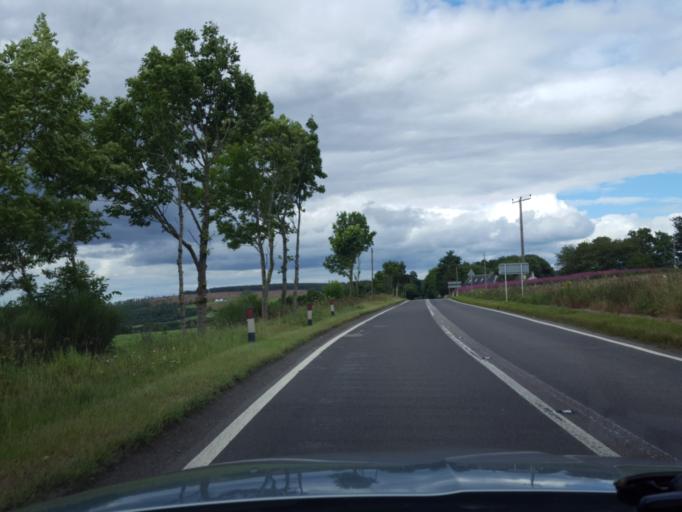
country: GB
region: Scotland
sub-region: Moray
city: Rothes
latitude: 57.4197
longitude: -3.3579
